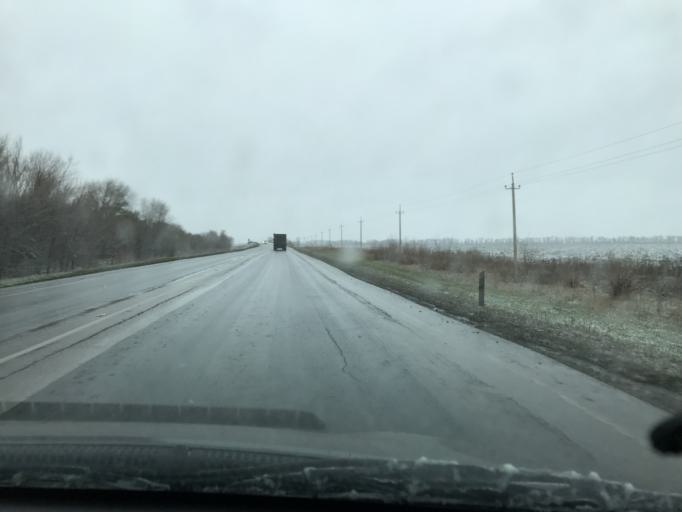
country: RU
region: Rostov
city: Mechetinskaya
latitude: 46.7686
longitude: 40.4246
